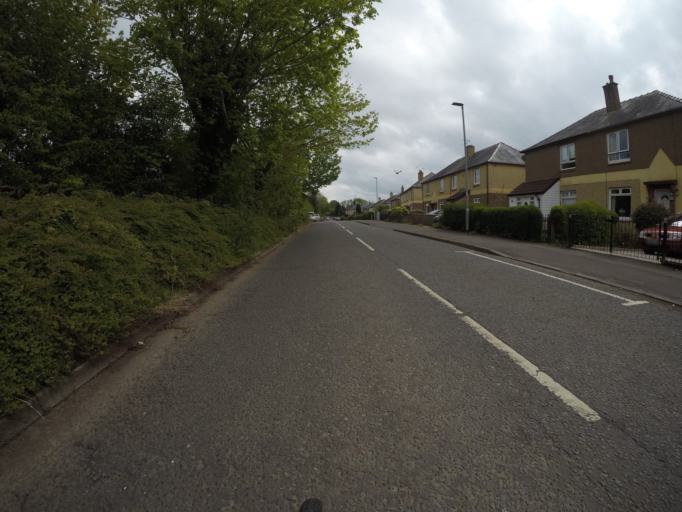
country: GB
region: Scotland
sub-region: North Ayrshire
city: Irvine
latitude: 55.6290
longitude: -4.6369
